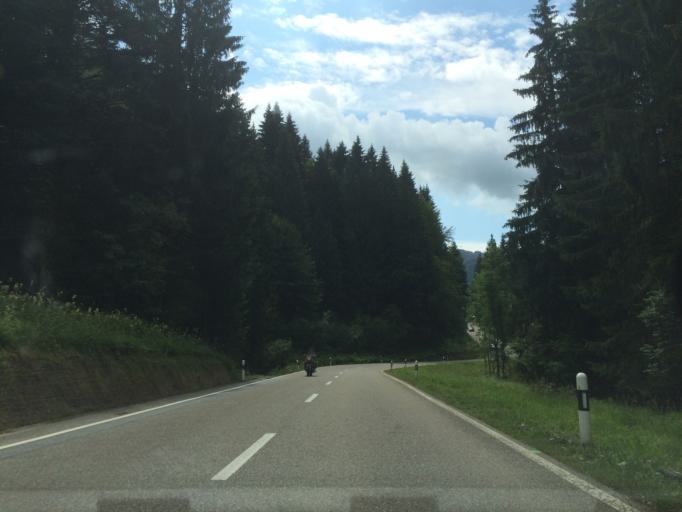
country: CH
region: Appenzell Ausserrhoden
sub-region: Bezirk Hinterland
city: Urnasch
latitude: 47.2592
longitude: 9.3100
